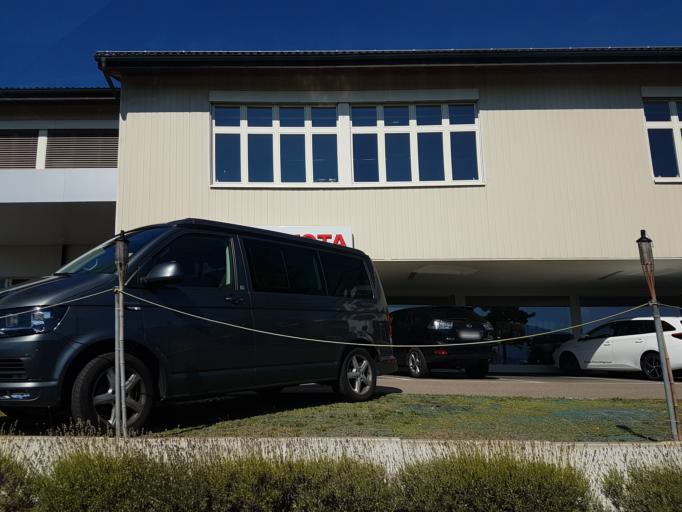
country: CH
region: Lucerne
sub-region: Lucerne-Land District
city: Udligenswil
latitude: 47.0870
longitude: 8.4001
